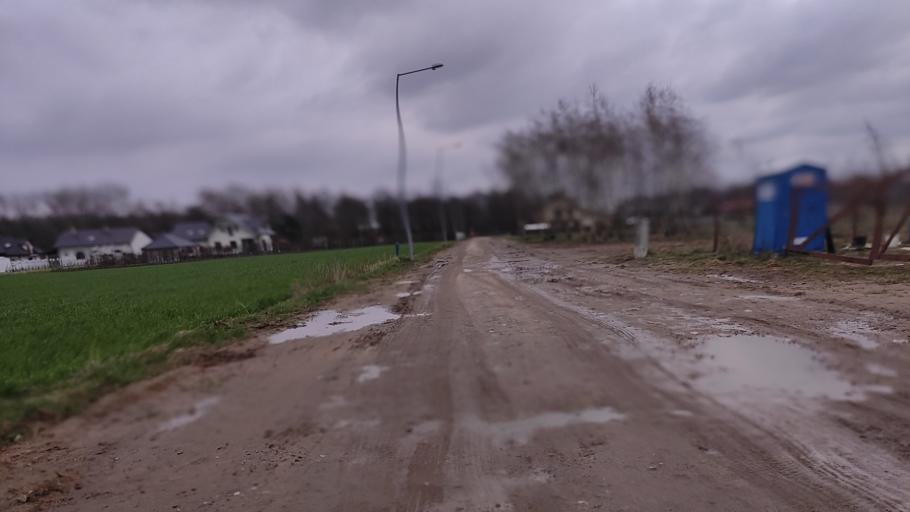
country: PL
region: Greater Poland Voivodeship
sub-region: Powiat poznanski
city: Kostrzyn
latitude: 52.4030
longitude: 17.1704
